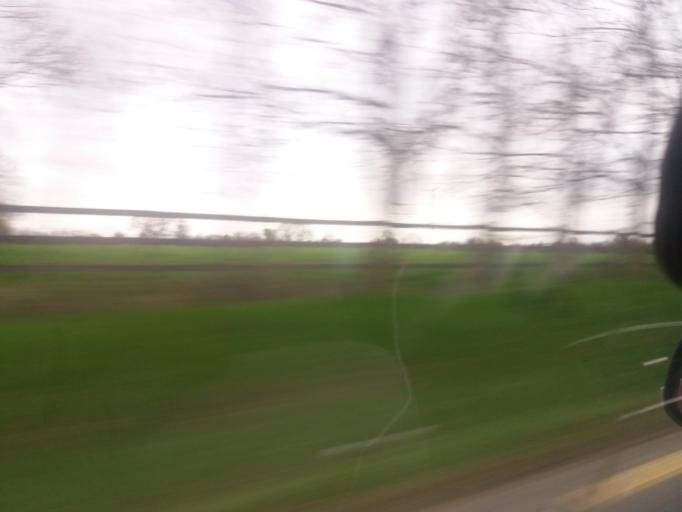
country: IE
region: Munster
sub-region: County Limerick
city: Adare
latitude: 52.5490
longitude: -8.8197
